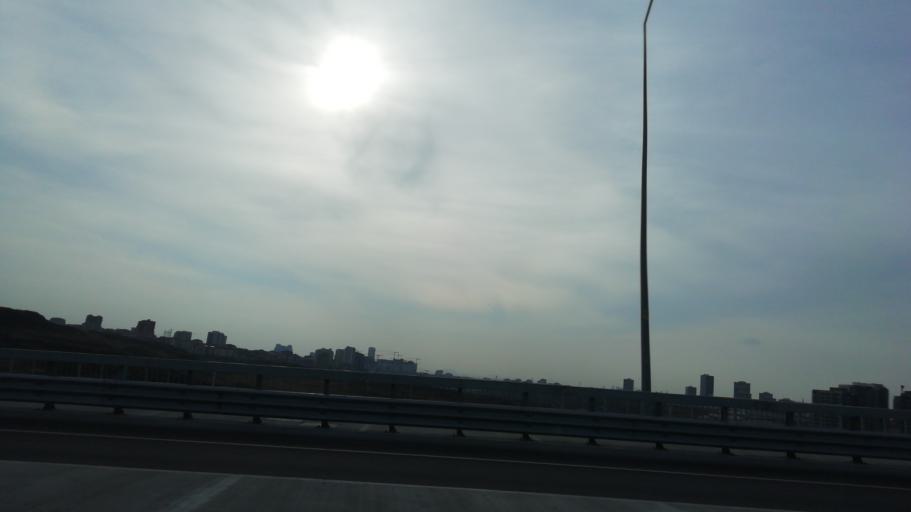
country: TR
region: Istanbul
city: Basaksehir
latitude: 41.1256
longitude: 28.7958
